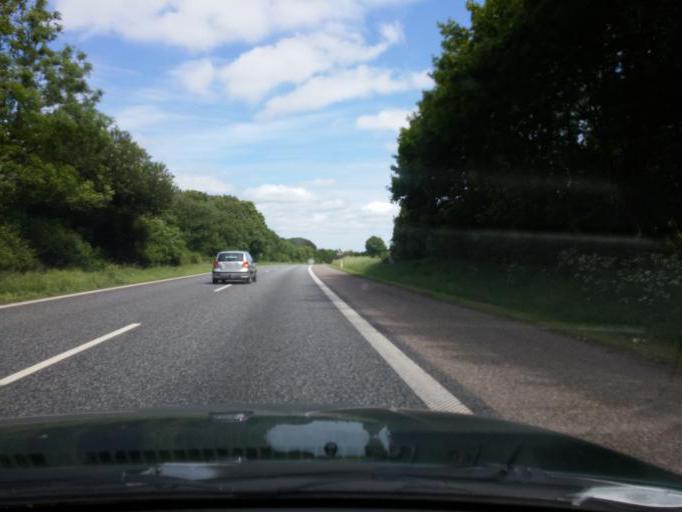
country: DK
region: South Denmark
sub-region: Fredericia Kommune
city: Taulov
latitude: 55.5461
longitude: 9.5333
